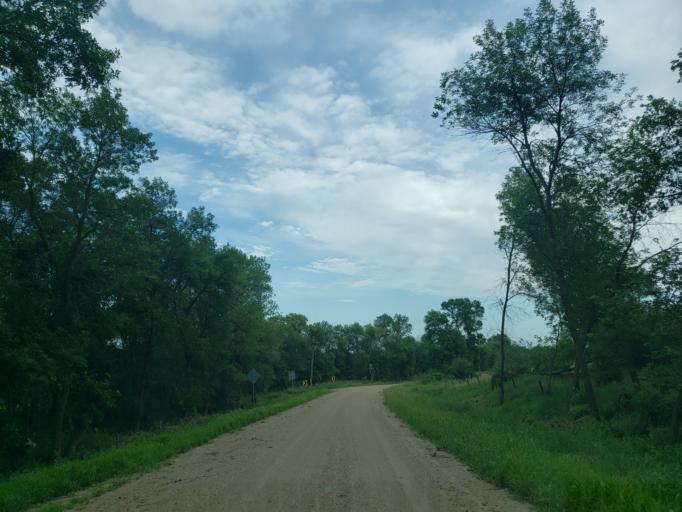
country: US
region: South Dakota
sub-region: Davison County
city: Mitchell
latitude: 43.6844
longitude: -97.9676
